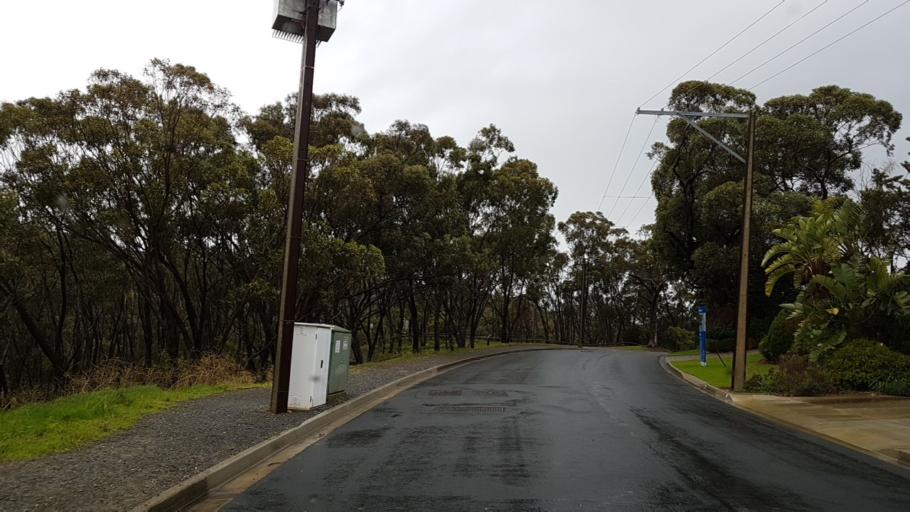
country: AU
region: South Australia
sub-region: Onkaparinga
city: Bedford Park
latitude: -35.0389
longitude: 138.5833
